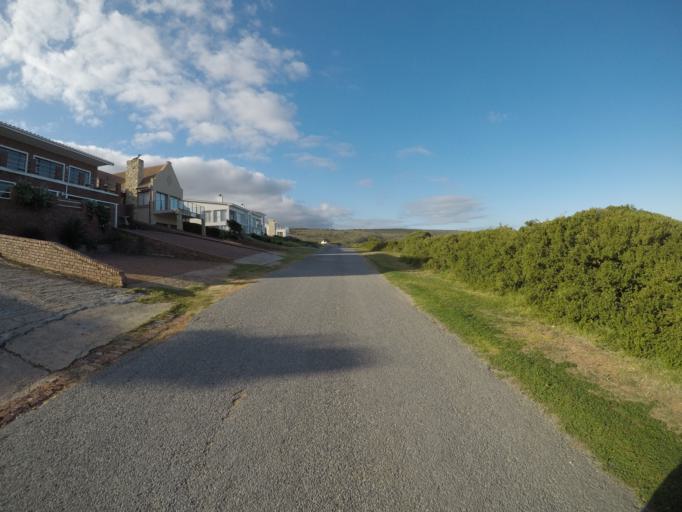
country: ZA
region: Western Cape
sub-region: Eden District Municipality
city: Riversdale
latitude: -34.4213
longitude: 21.3488
